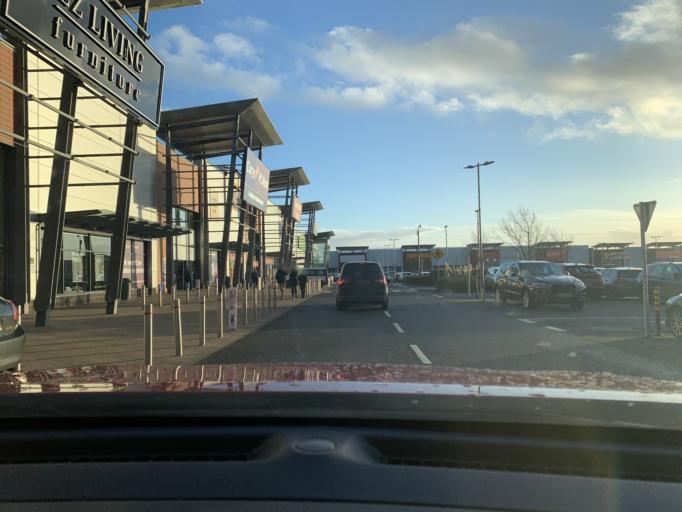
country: IE
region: Connaught
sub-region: Sligo
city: Sligo
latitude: 54.2511
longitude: -8.4703
